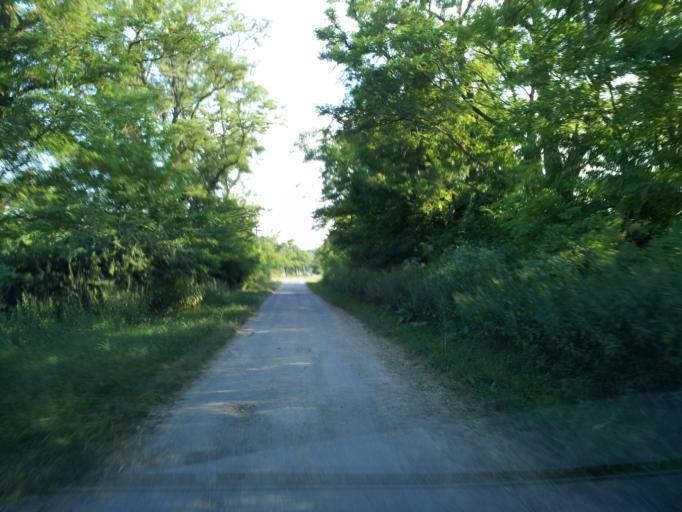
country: HU
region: Fejer
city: Many
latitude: 47.5652
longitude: 18.5982
